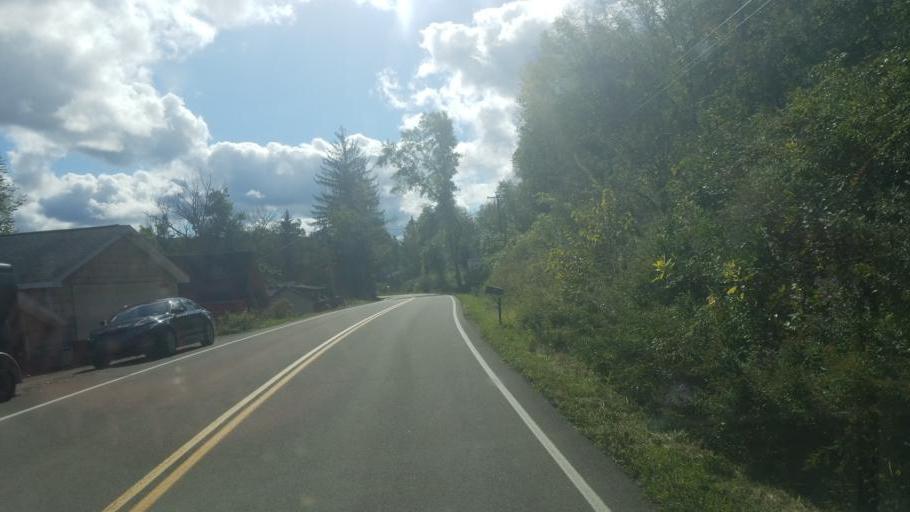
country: US
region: New York
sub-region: Allegany County
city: Cuba
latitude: 42.2451
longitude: -78.2785
